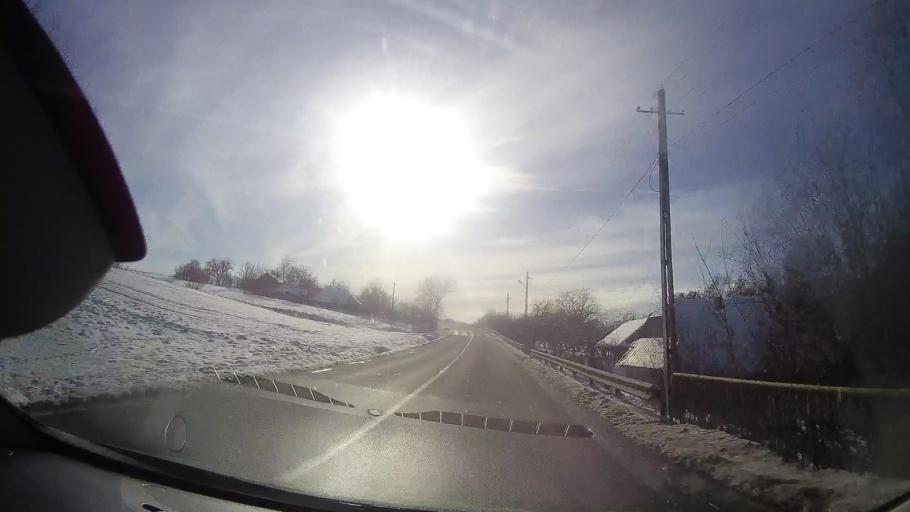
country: RO
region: Neamt
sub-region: Comuna Baltatesti
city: Valea Seaca
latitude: 47.1654
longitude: 26.3190
